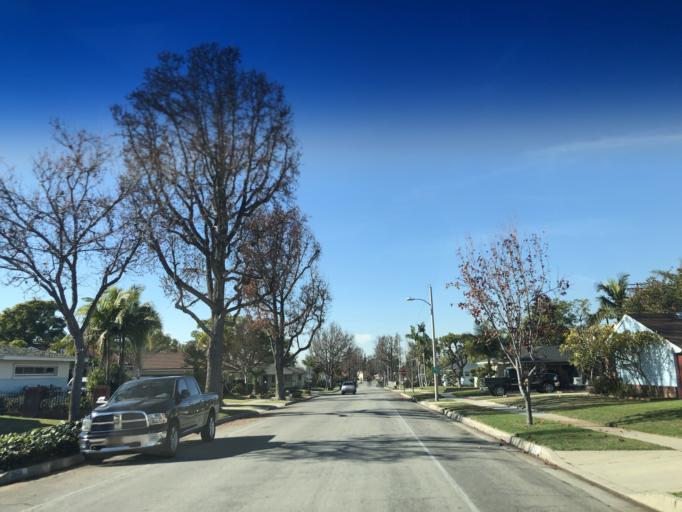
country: US
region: California
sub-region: Los Angeles County
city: East La Mirada
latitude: 33.9416
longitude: -117.9970
